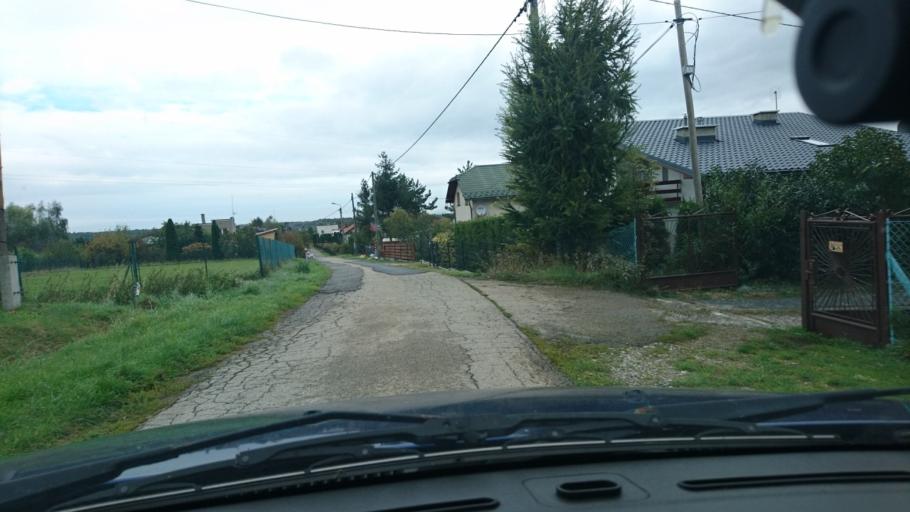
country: PL
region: Silesian Voivodeship
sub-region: Powiat bielski
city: Bujakow
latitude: 49.8460
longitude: 19.1769
